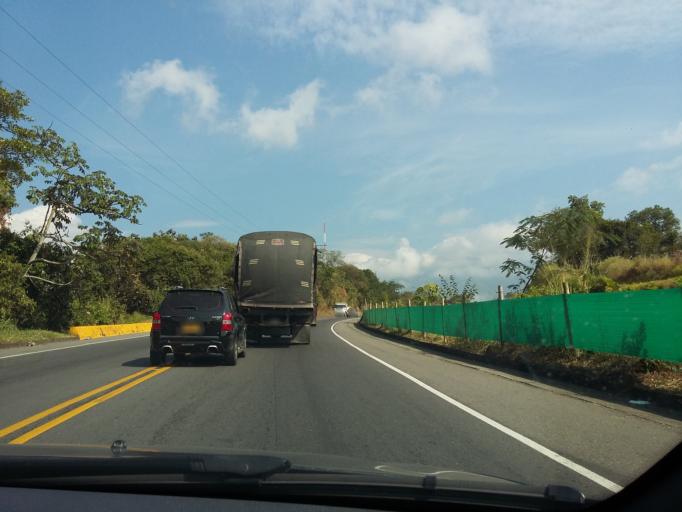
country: CO
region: Tolima
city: Ibague
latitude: 4.4090
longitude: -75.1855
